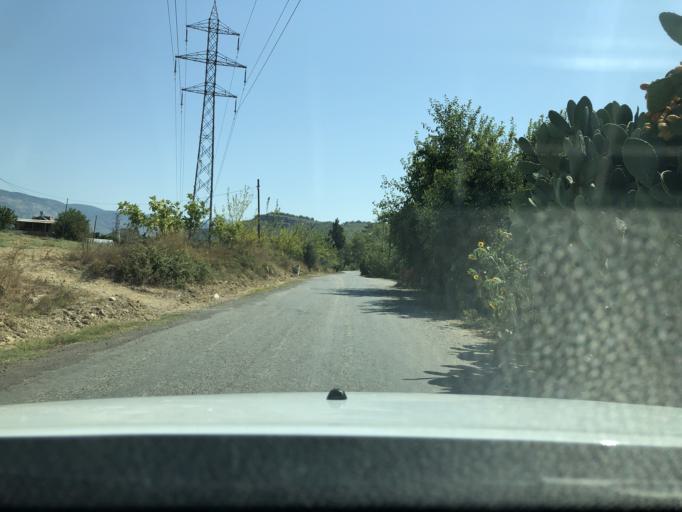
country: TR
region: Antalya
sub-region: Manavgat
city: Manavgat
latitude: 36.8217
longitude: 31.5042
